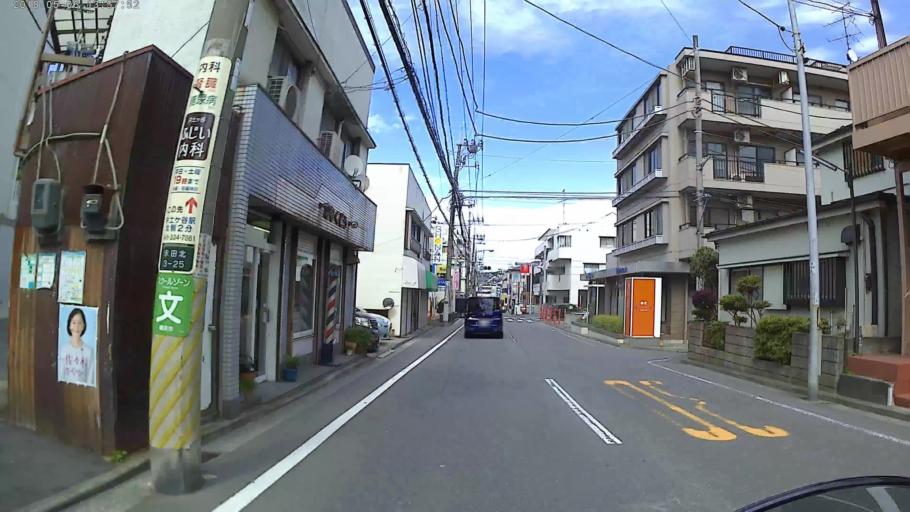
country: JP
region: Kanagawa
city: Yokohama
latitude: 35.4379
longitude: 139.5871
